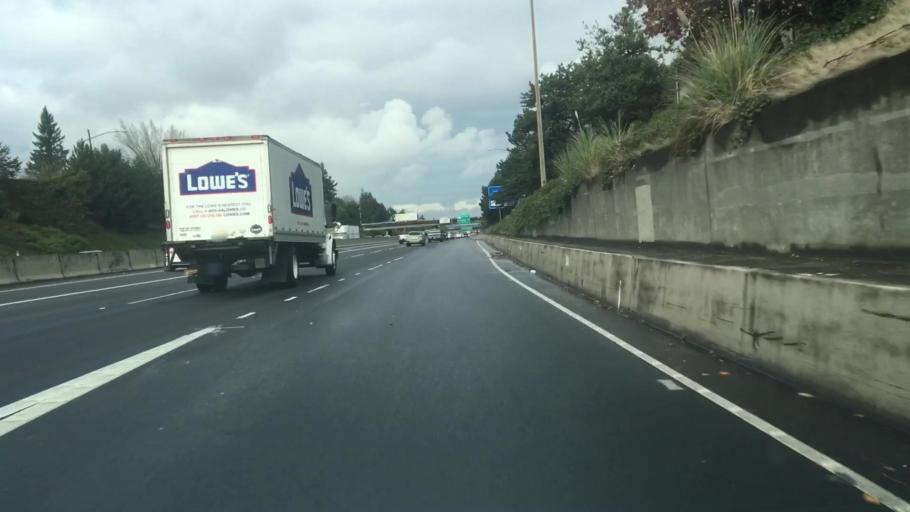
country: US
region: Oregon
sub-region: Multnomah County
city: Portland
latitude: 45.5634
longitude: -122.6784
